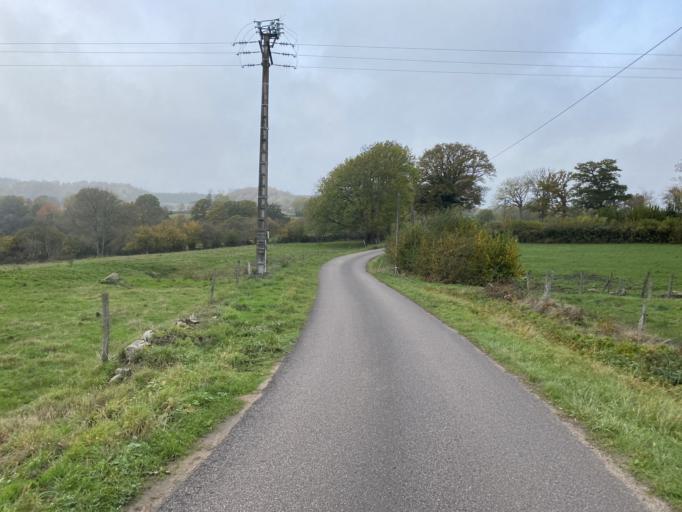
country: FR
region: Bourgogne
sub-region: Departement de la Cote-d'Or
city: Saulieu
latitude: 47.2708
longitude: 4.1819
